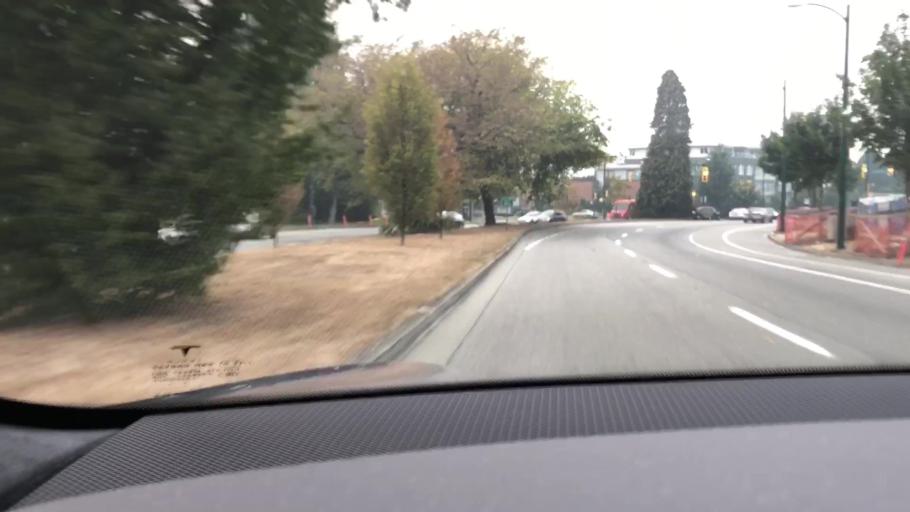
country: CA
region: British Columbia
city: Vancouver
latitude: 49.2401
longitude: -123.1178
